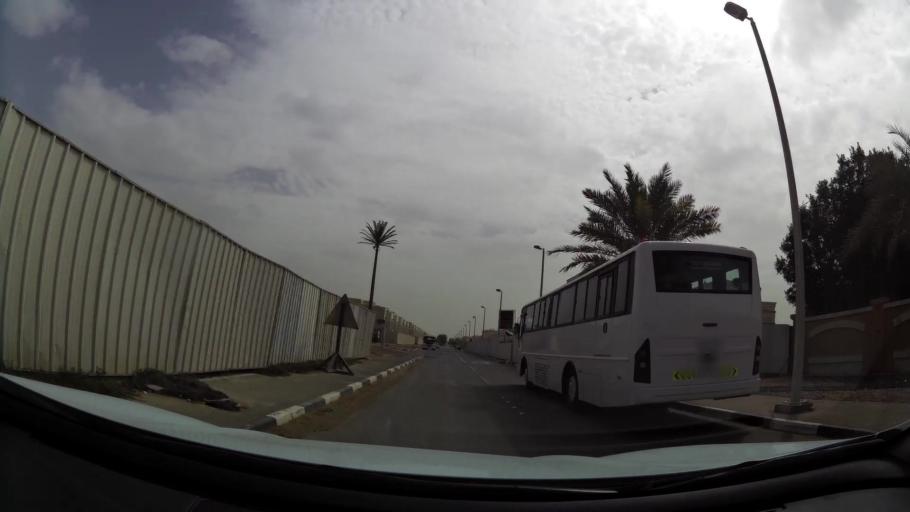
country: AE
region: Abu Dhabi
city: Abu Dhabi
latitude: 24.3988
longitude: 54.4869
